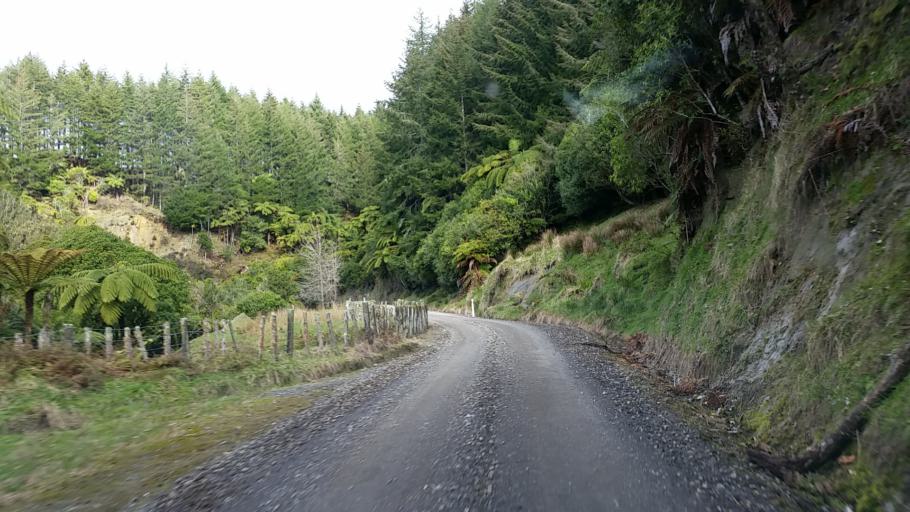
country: NZ
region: Taranaki
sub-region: South Taranaki District
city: Eltham
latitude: -39.1723
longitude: 174.6147
